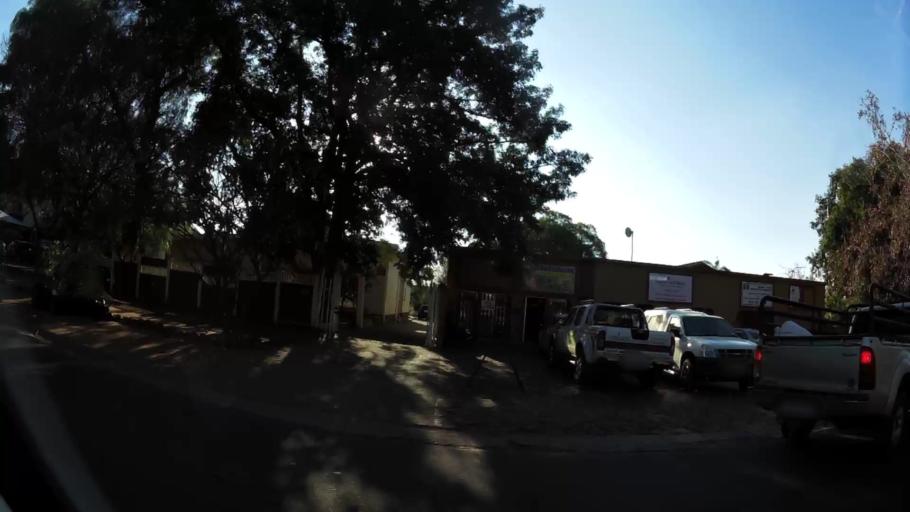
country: ZA
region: North-West
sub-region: Bojanala Platinum District Municipality
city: Rustenburg
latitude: -25.6757
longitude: 27.2366
